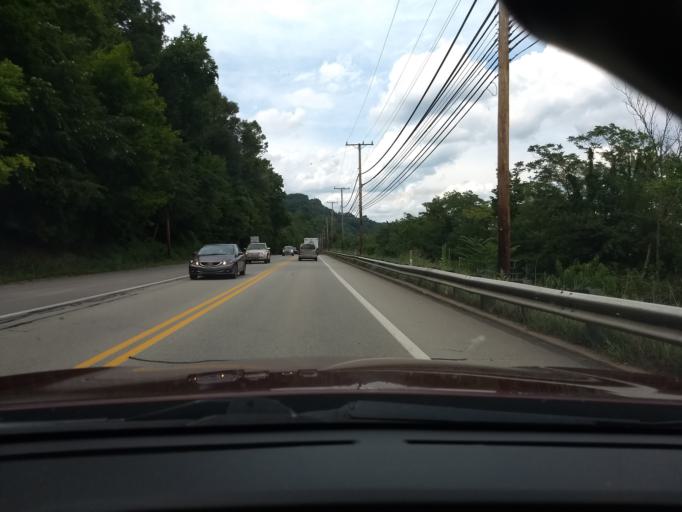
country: US
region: Pennsylvania
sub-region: Allegheny County
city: Verona
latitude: 40.5109
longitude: -79.8523
